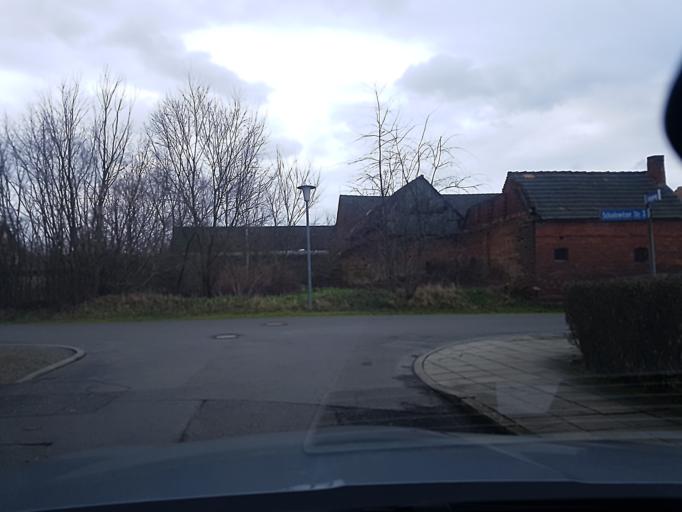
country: DE
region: Brandenburg
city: Trobitz
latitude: 51.5946
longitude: 13.4301
